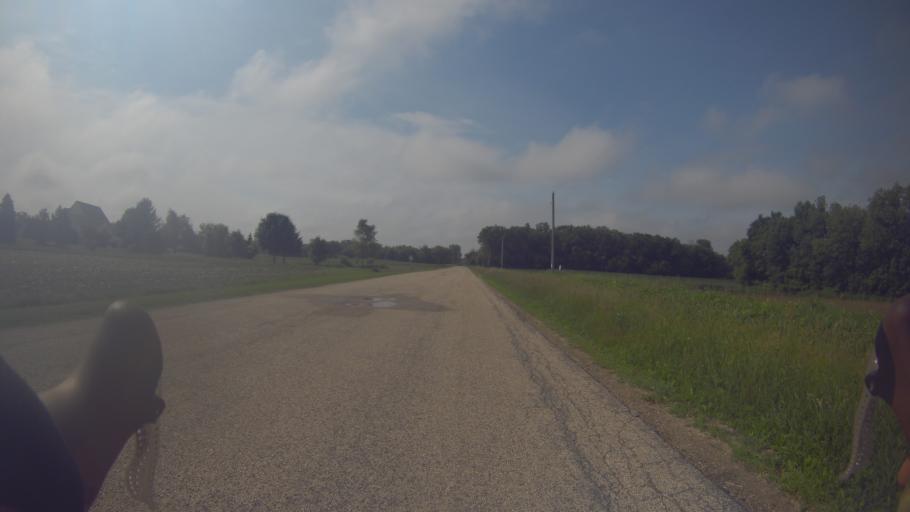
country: US
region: Wisconsin
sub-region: Dane County
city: Stoughton
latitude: 42.9514
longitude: -89.1810
